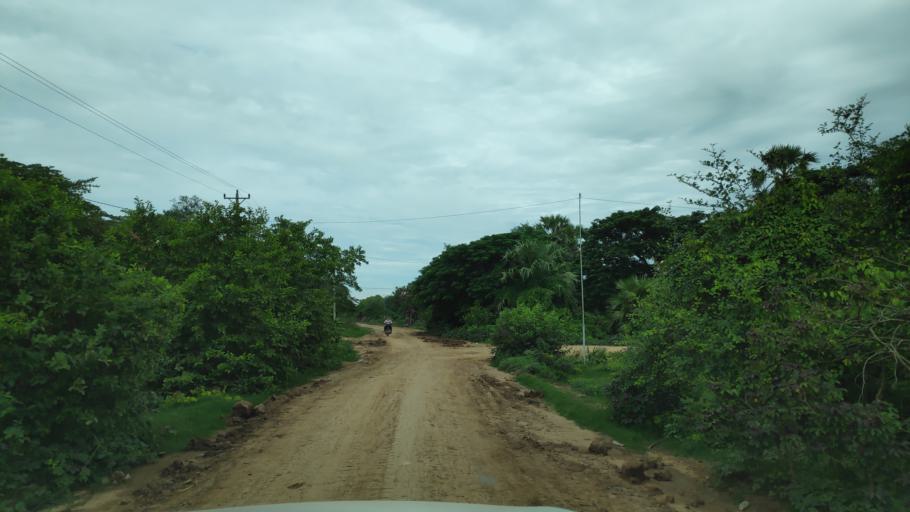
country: KH
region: Kampong Cham
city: Kampong Cham
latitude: 11.9388
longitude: 105.0881
